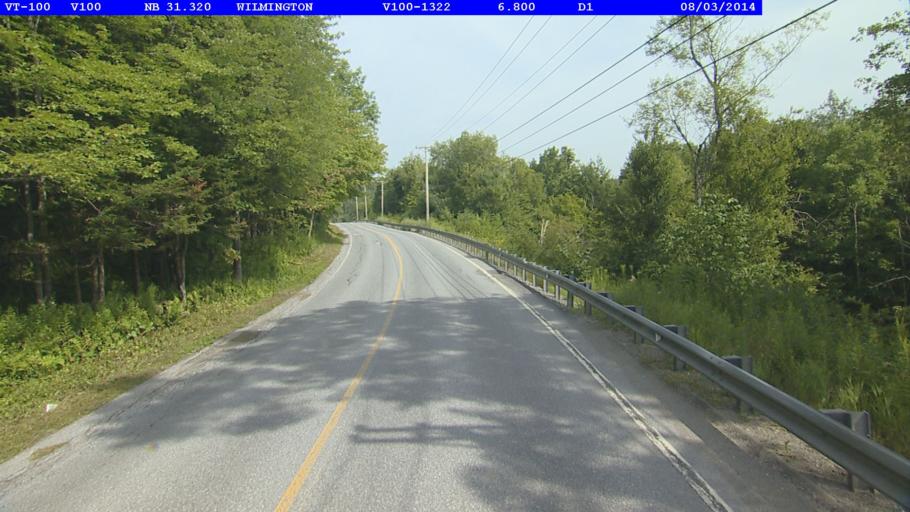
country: US
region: Vermont
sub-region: Windham County
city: Dover
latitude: 42.9191
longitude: -72.8406
